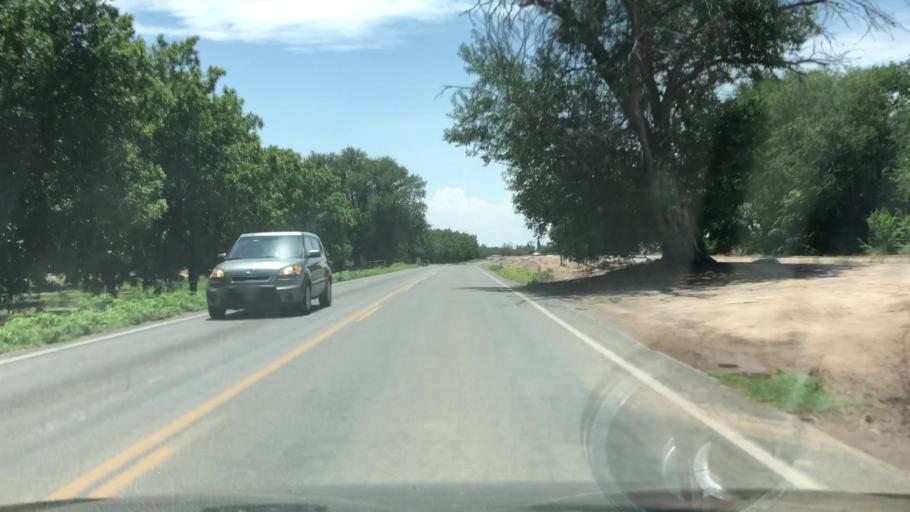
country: US
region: New Mexico
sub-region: Dona Ana County
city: Anthony
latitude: 32.0162
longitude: -106.6679
